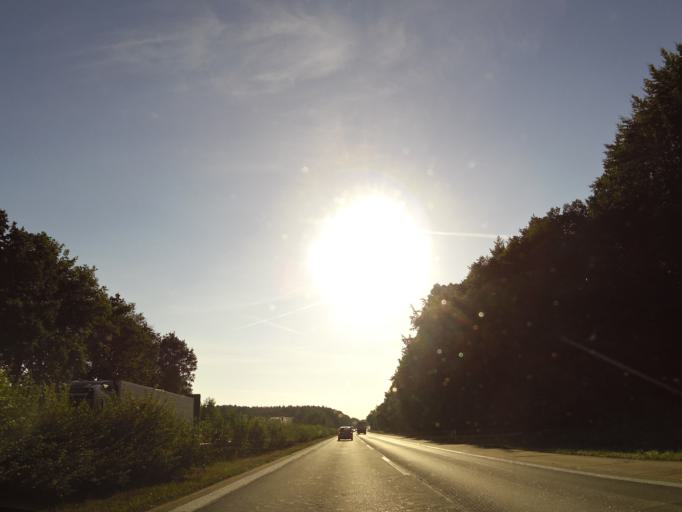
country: DE
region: Bavaria
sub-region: Regierungsbezirk Mittelfranken
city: Muhlhausen
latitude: 49.7348
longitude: 10.7494
